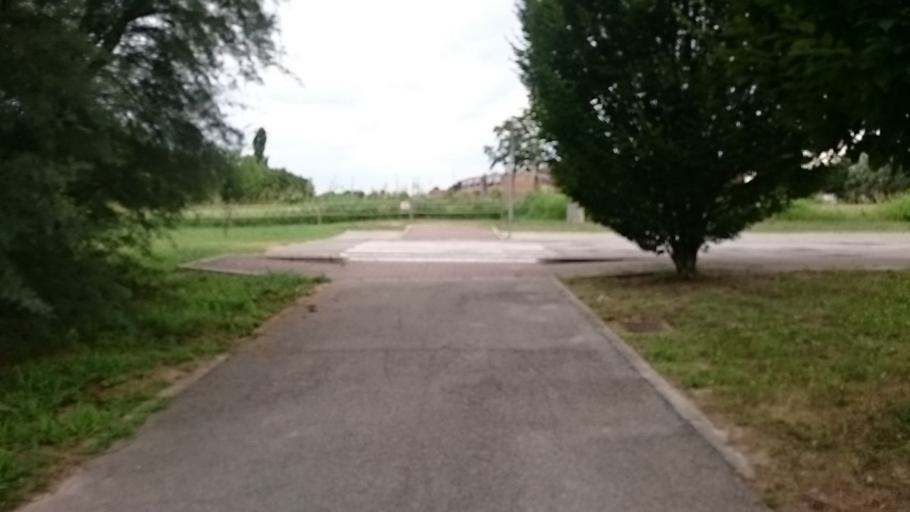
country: IT
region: Veneto
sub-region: Provincia di Padova
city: Albignasego
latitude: 45.3472
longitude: 11.8755
